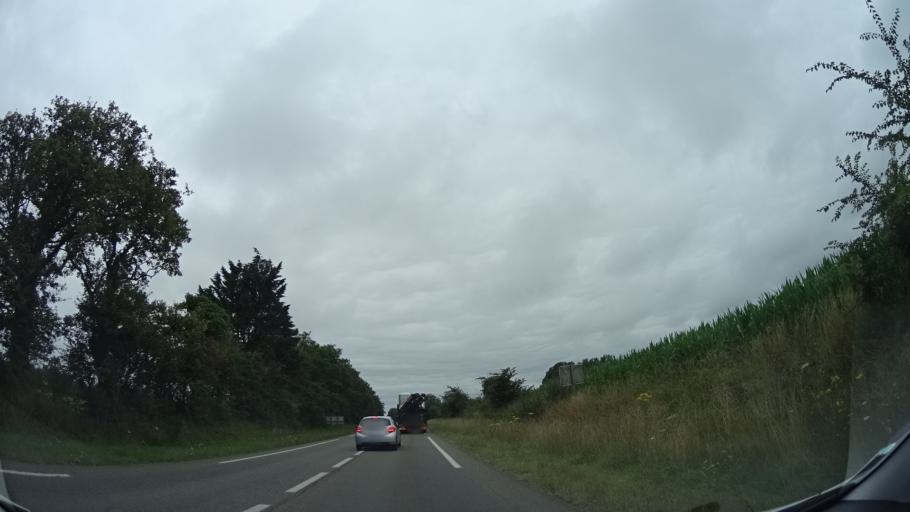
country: FR
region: Lower Normandy
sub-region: Departement de la Manche
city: Portbail
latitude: 49.3620
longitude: -1.6980
